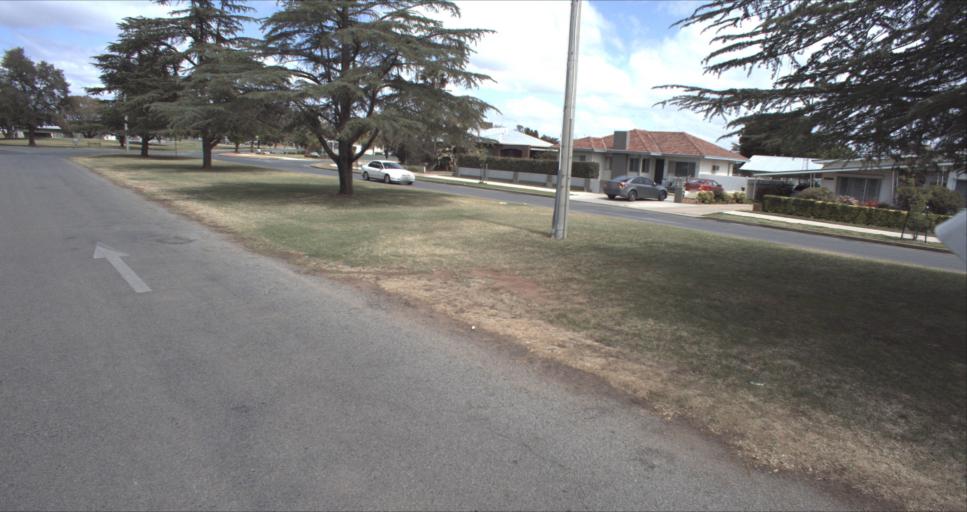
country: AU
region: New South Wales
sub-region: Leeton
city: Leeton
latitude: -34.5596
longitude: 146.3979
